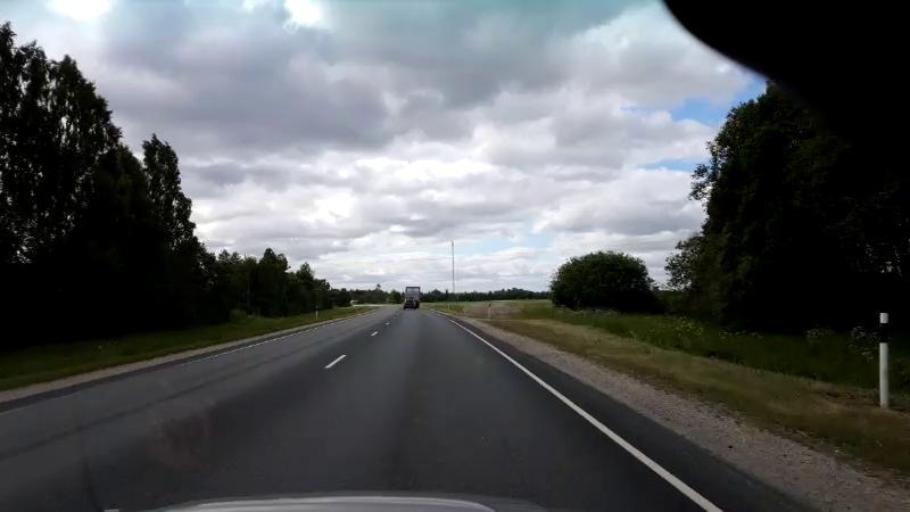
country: EE
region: Raplamaa
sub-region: Maerjamaa vald
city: Marjamaa
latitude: 58.7736
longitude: 24.4144
